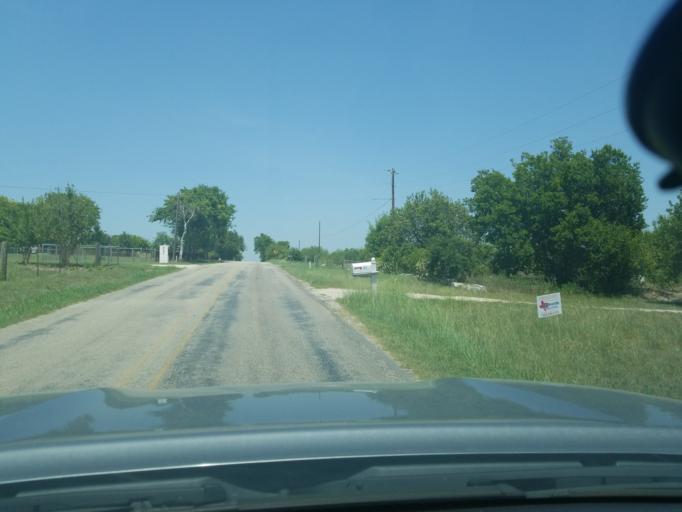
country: US
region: Texas
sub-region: Guadalupe County
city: Cibolo
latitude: 29.5848
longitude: -98.2060
